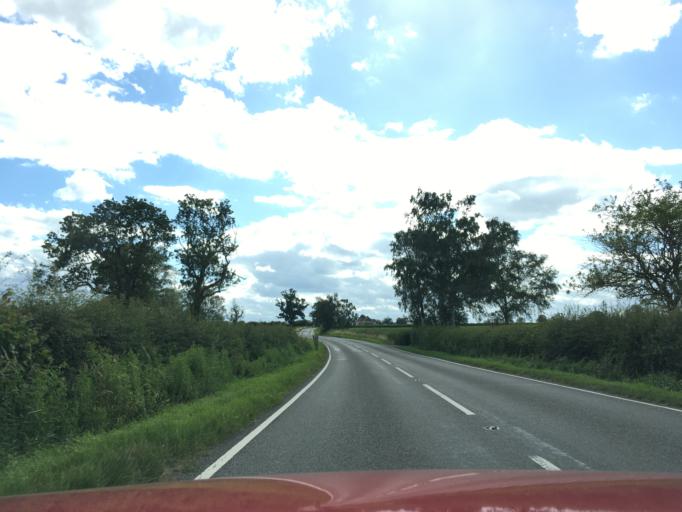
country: GB
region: England
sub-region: Leicestershire
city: Shepshed
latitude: 52.7872
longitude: -1.3185
